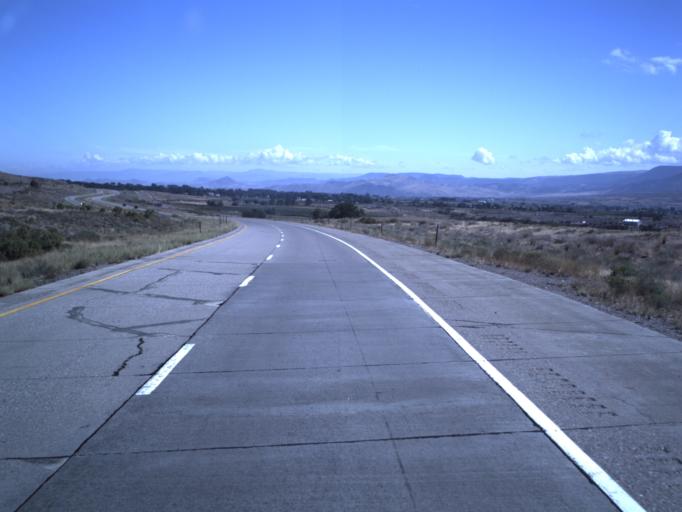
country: US
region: Utah
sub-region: Sevier County
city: Monroe
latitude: 38.6606
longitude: -112.1792
